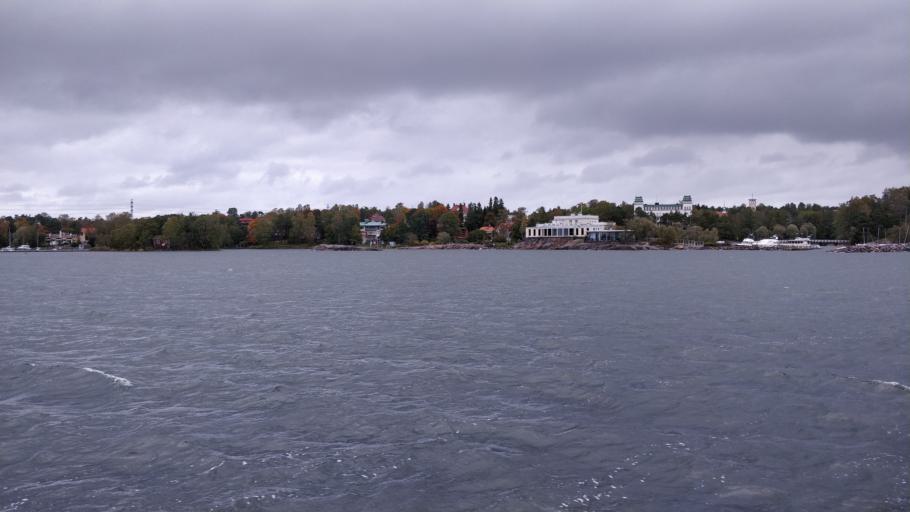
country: FI
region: Uusimaa
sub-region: Helsinki
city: Helsinki
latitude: 60.1781
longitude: 25.0054
